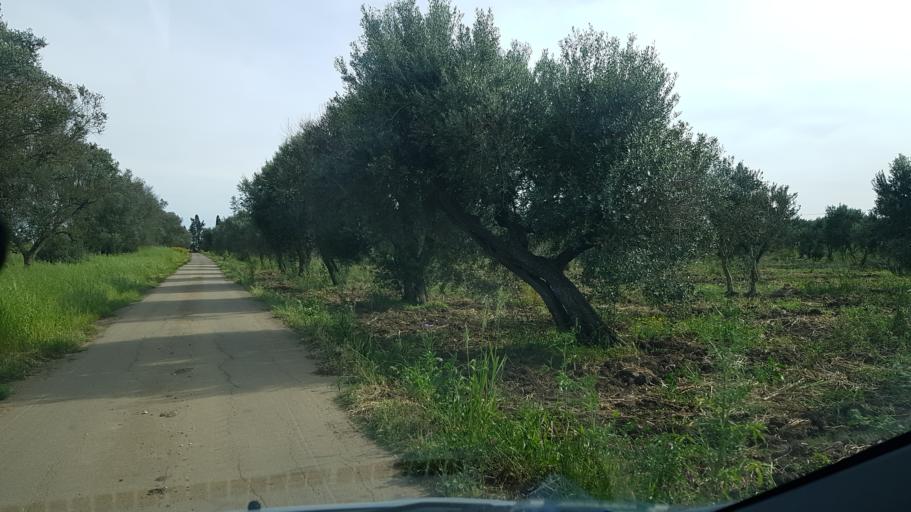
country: IT
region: Apulia
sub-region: Provincia di Brindisi
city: Tuturano
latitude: 40.5642
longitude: 17.9178
